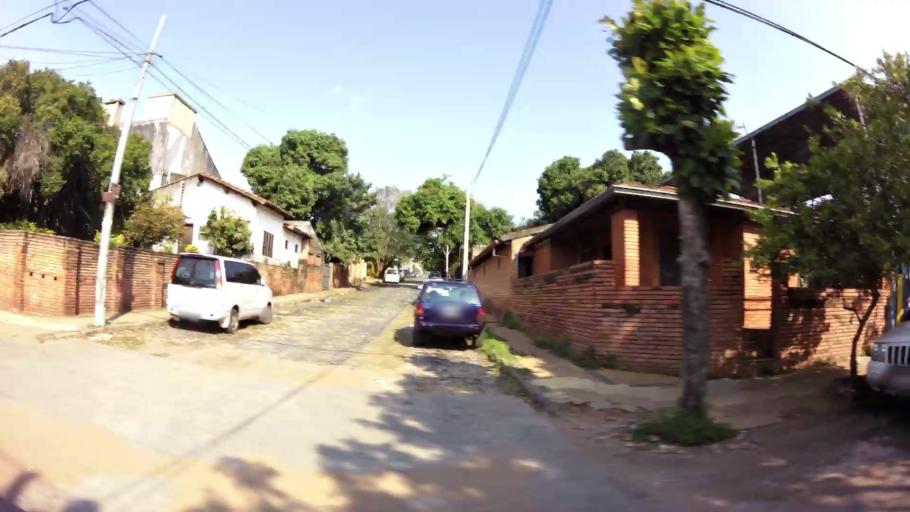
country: PY
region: Asuncion
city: Asuncion
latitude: -25.3127
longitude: -57.6268
